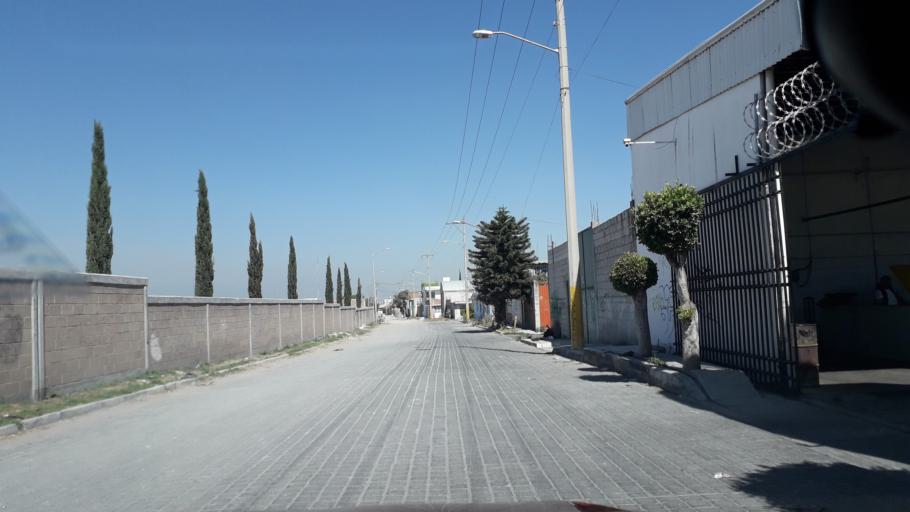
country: MX
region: Puebla
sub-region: Cuautlancingo
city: Sanctorum
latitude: 19.0849
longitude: -98.2162
